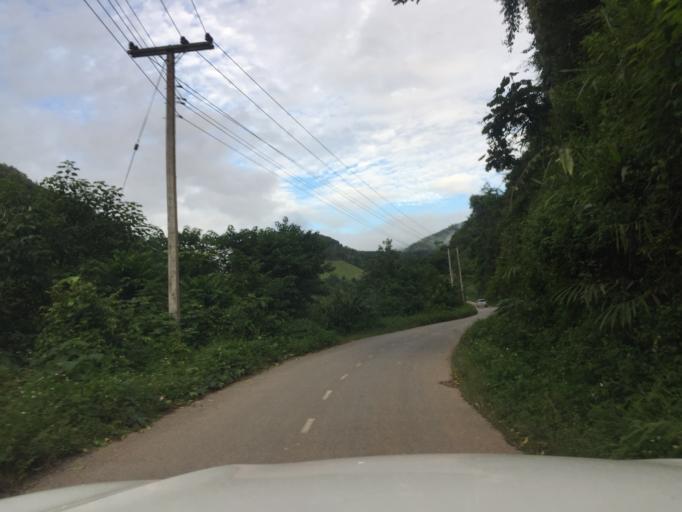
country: LA
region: Phongsali
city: Khoa
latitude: 21.1034
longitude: 102.3024
